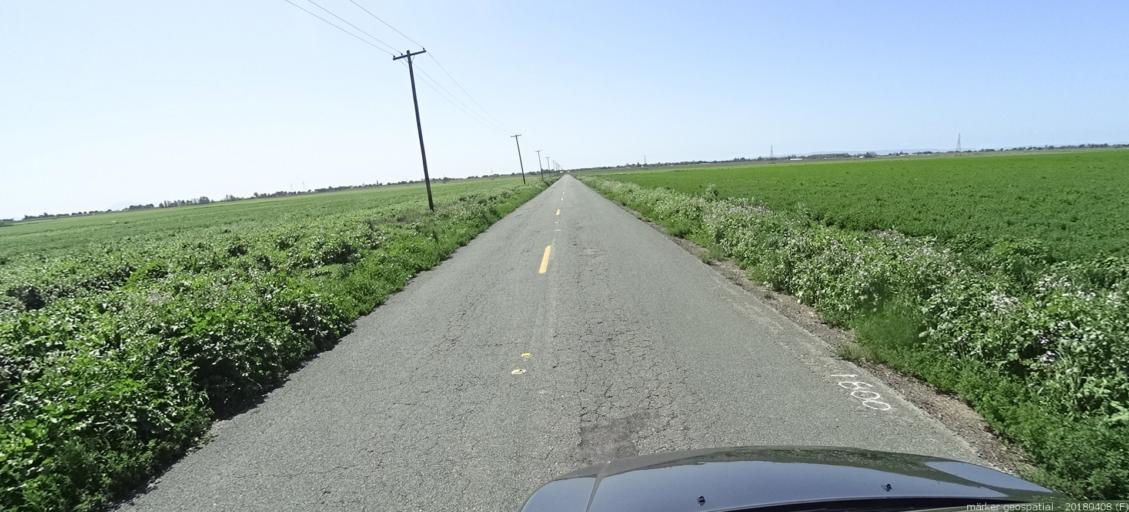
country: US
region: California
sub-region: Sacramento County
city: Walnut Grove
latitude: 38.3095
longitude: -121.5376
